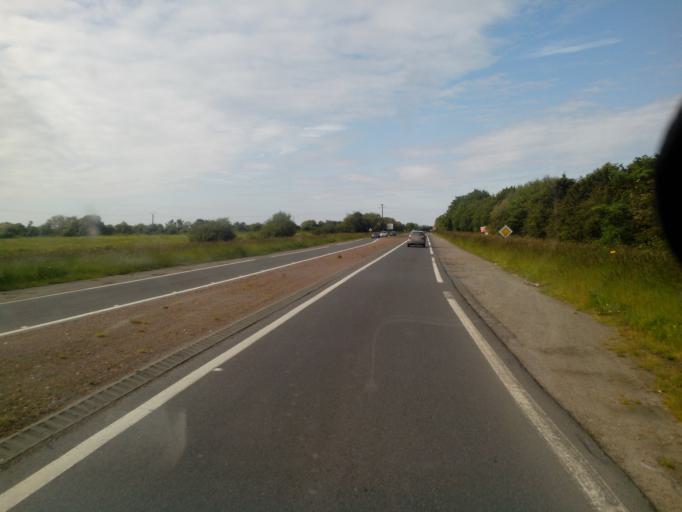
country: FR
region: Lower Normandy
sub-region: Departement du Calvados
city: Dives-sur-Mer
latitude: 49.2581
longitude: -0.1039
